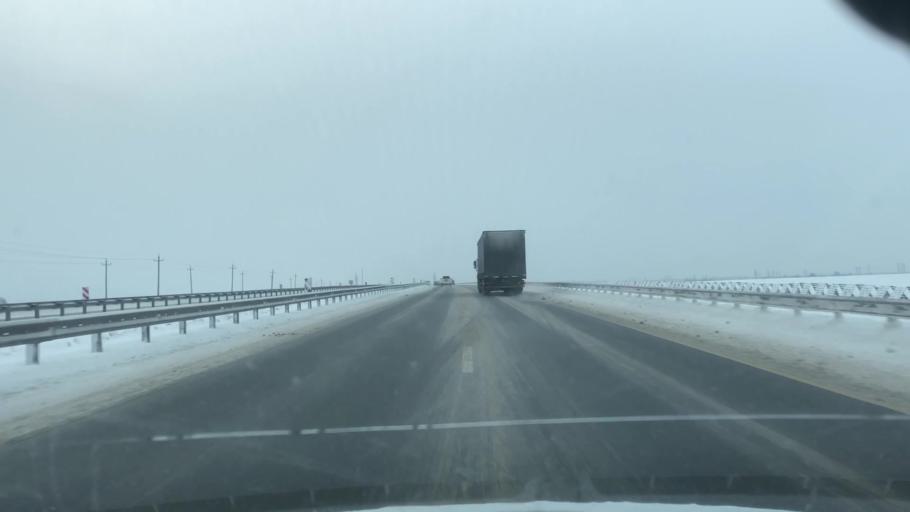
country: RU
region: Moskovskaya
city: Mikhnevo
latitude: 55.1081
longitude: 37.9261
